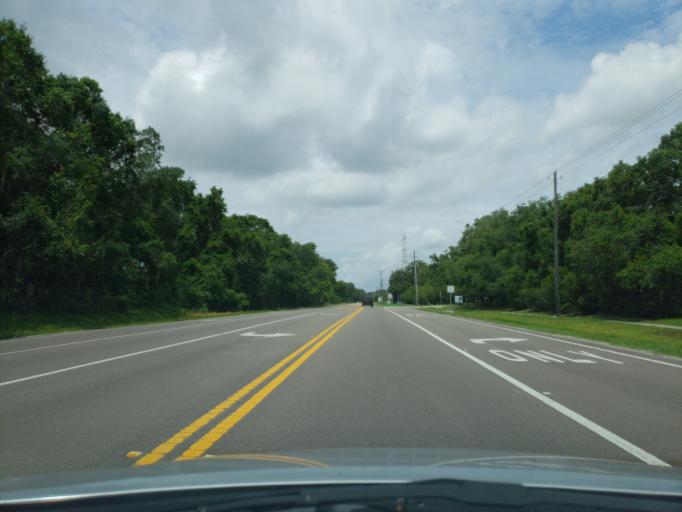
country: US
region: Florida
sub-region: Hillsborough County
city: East Lake-Orient Park
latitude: 28.0110
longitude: -82.3579
